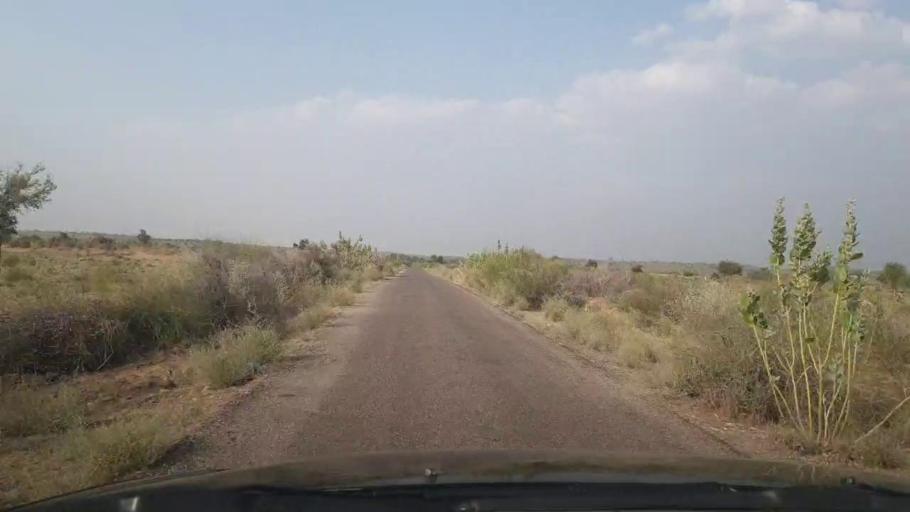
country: PK
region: Sindh
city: Islamkot
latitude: 25.0593
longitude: 70.5611
